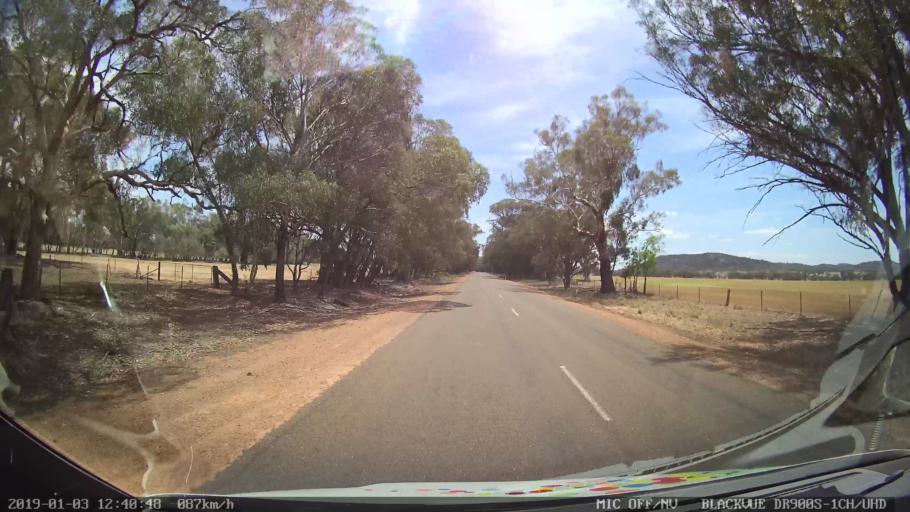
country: AU
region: New South Wales
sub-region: Weddin
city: Grenfell
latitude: -33.8080
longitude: 148.2136
